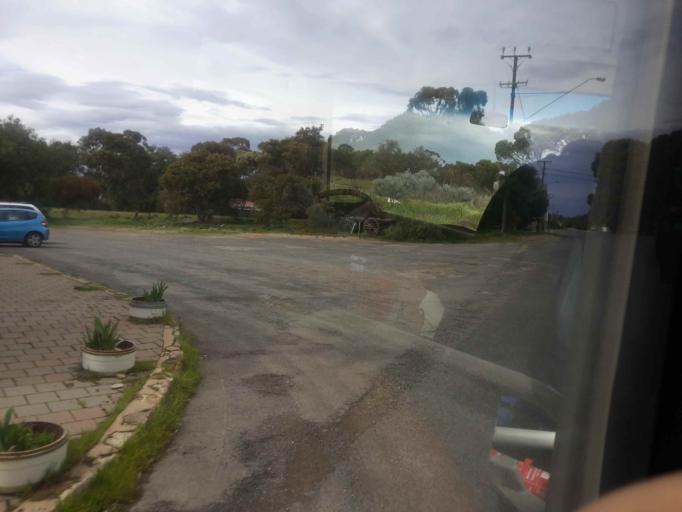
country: AU
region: South Australia
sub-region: Clare and Gilbert Valleys
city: Clare
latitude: -33.6714
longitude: 138.9222
